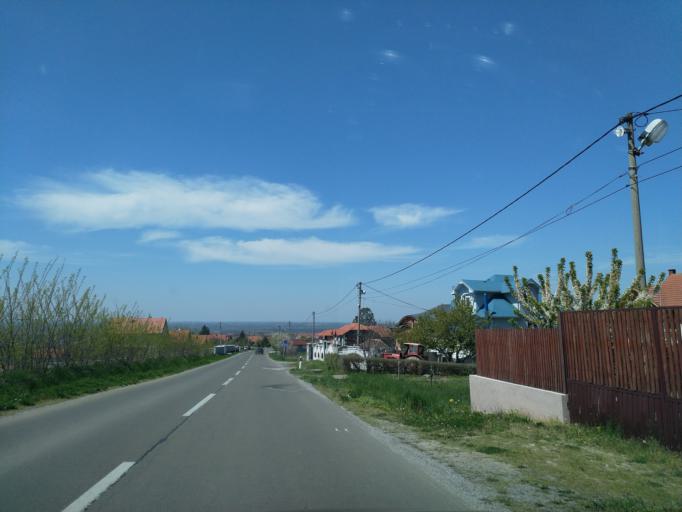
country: RS
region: Central Serbia
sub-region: Belgrade
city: Lazarevac
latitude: 44.3725
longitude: 20.3002
